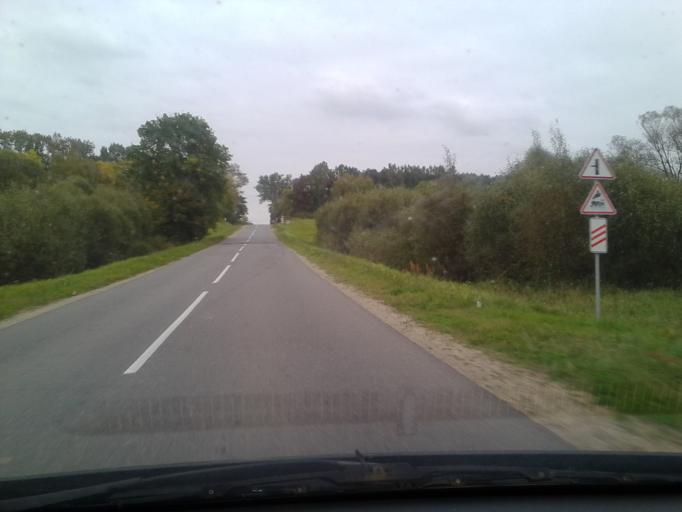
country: BY
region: Vitebsk
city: Pastavy
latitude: 55.1284
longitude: 26.9350
